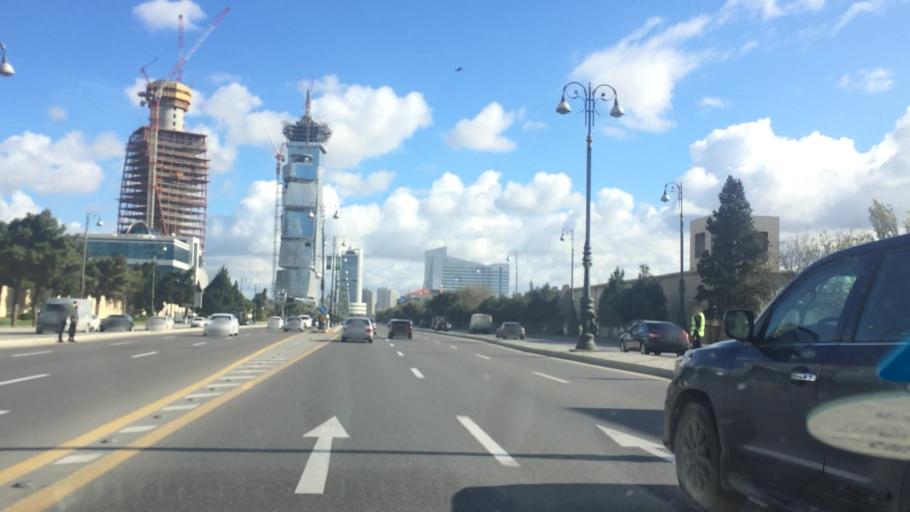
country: AZ
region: Baki
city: Baku
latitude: 40.4067
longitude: 49.8903
